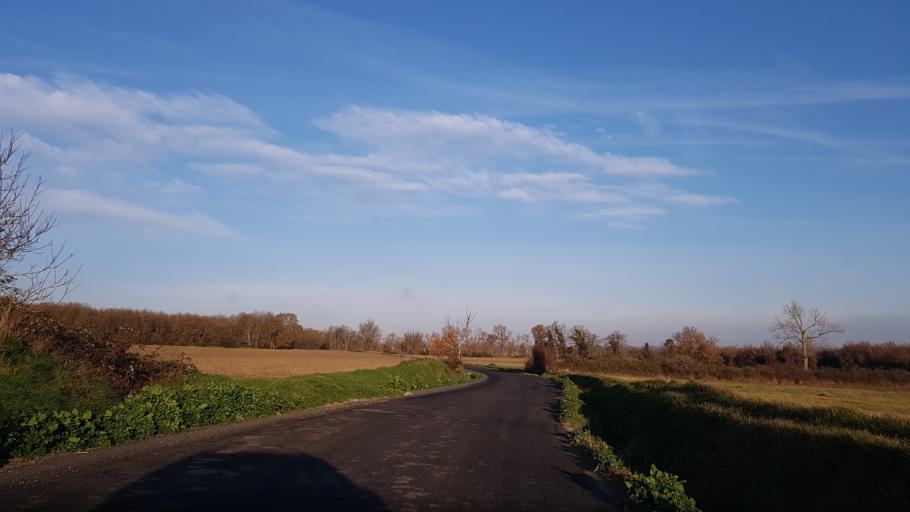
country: FR
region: Languedoc-Roussillon
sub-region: Departement de l'Aude
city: Villeneuve-la-Comptal
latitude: 43.2815
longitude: 1.9373
